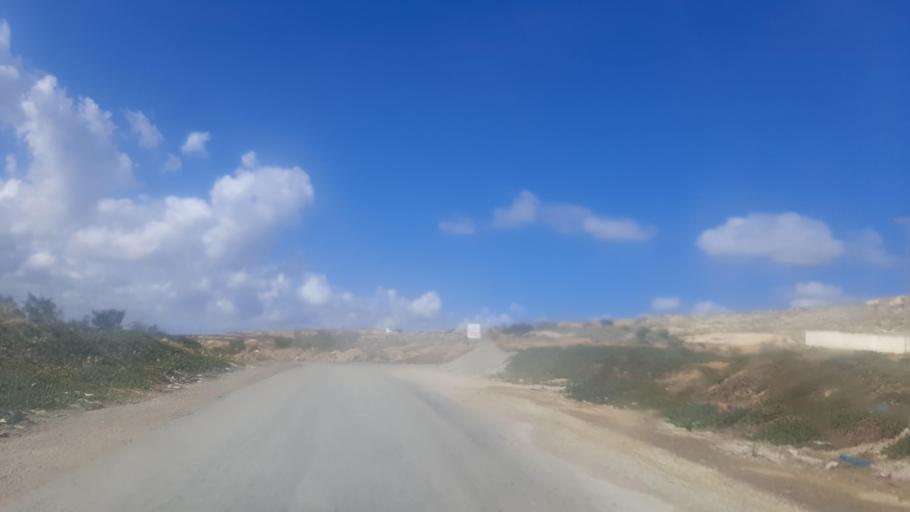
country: TN
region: Nabul
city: Nabeul
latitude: 36.4925
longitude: 10.7059
